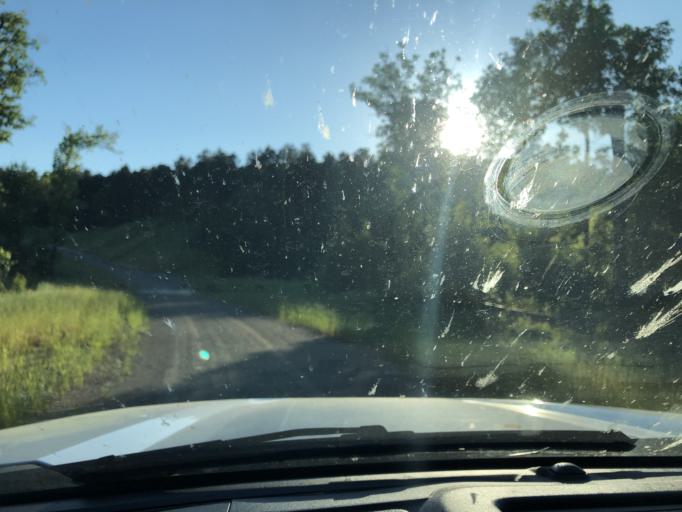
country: US
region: Oklahoma
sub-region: Le Flore County
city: Talihina
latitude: 34.5813
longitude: -95.1685
